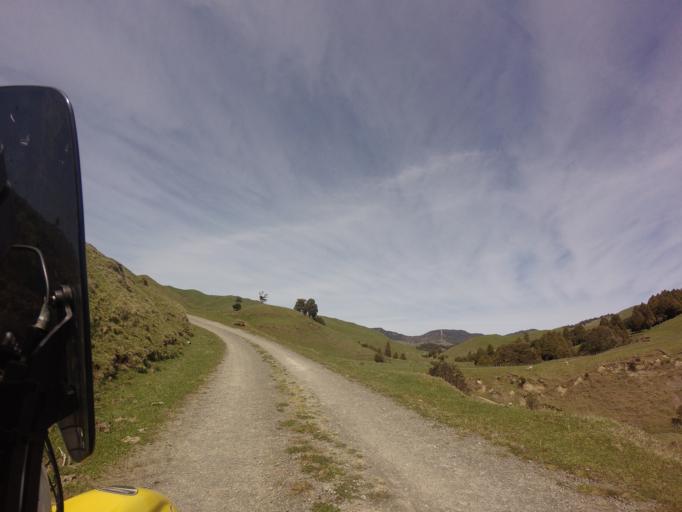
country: NZ
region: Bay of Plenty
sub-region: Opotiki District
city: Opotiki
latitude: -38.4556
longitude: 177.3480
